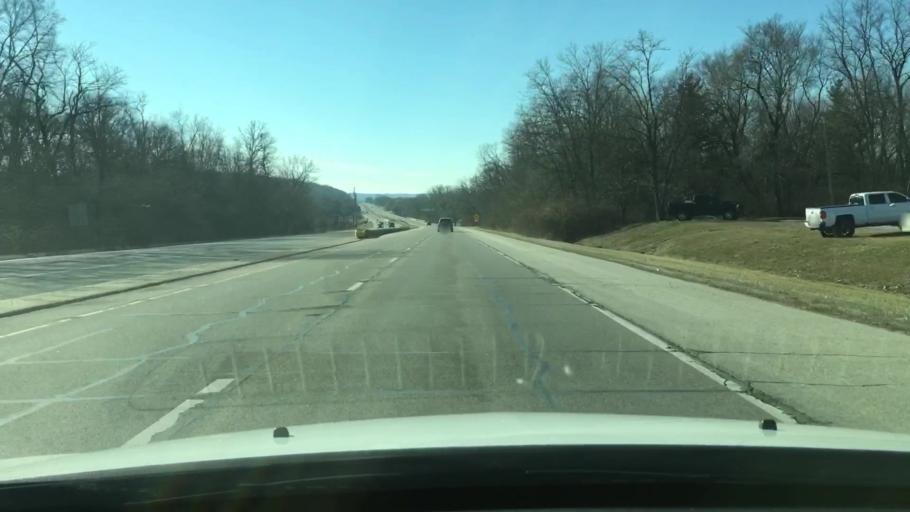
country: US
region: Illinois
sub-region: Woodford County
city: Germantown Hills
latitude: 40.7434
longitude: -89.5124
